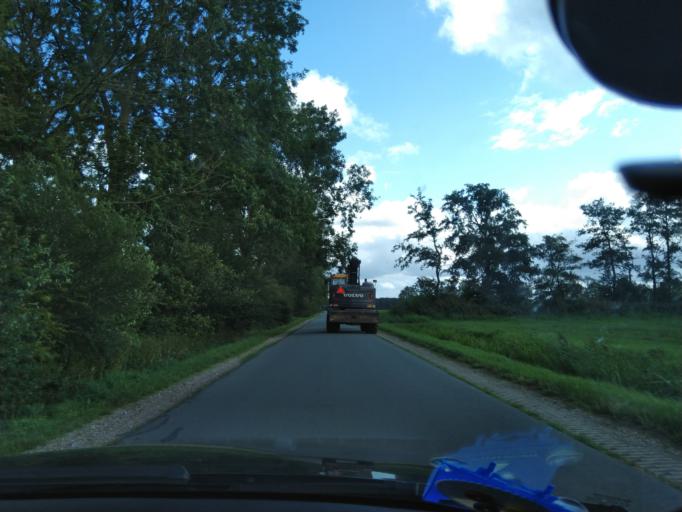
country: NL
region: Drenthe
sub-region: Gemeente Tynaarlo
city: Vries
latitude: 53.0875
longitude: 6.5361
